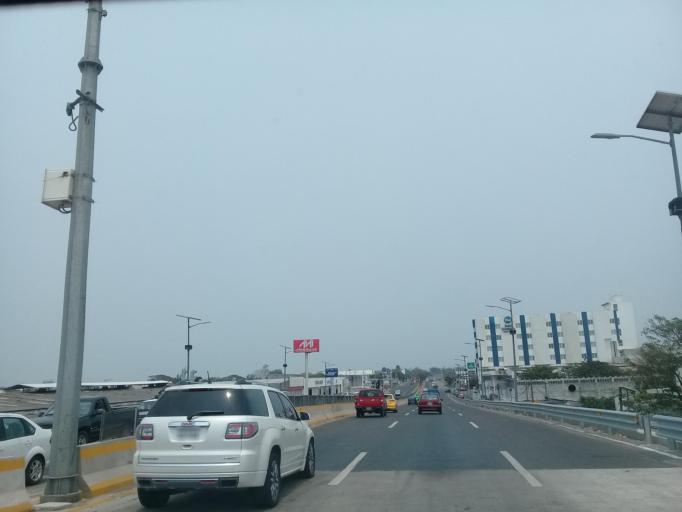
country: MX
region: Veracruz
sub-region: Veracruz
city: Las Amapolas
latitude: 19.1577
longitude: -96.1947
